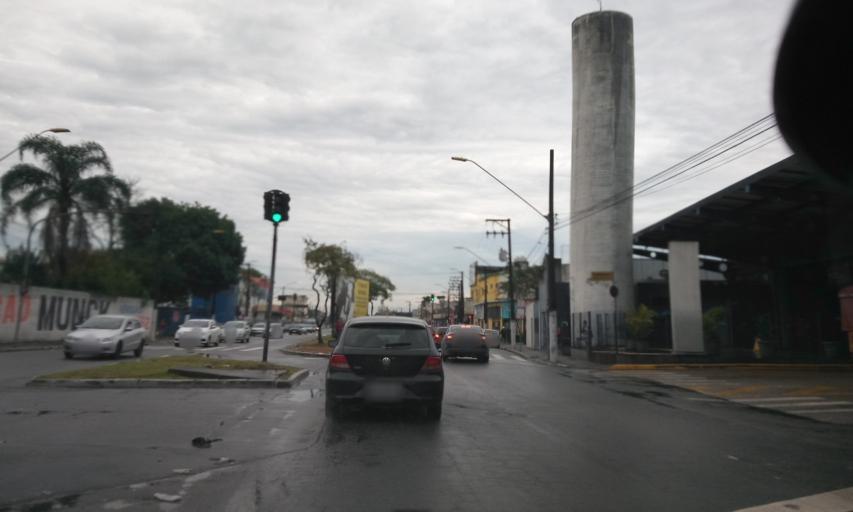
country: BR
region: Sao Paulo
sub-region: Santo Andre
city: Santo Andre
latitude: -23.6994
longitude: -46.5059
